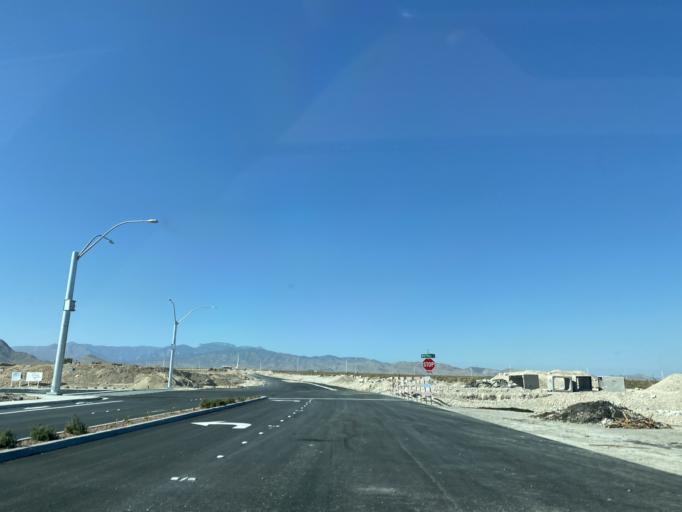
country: US
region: Nevada
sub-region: Clark County
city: Summerlin South
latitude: 36.3213
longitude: -115.3142
